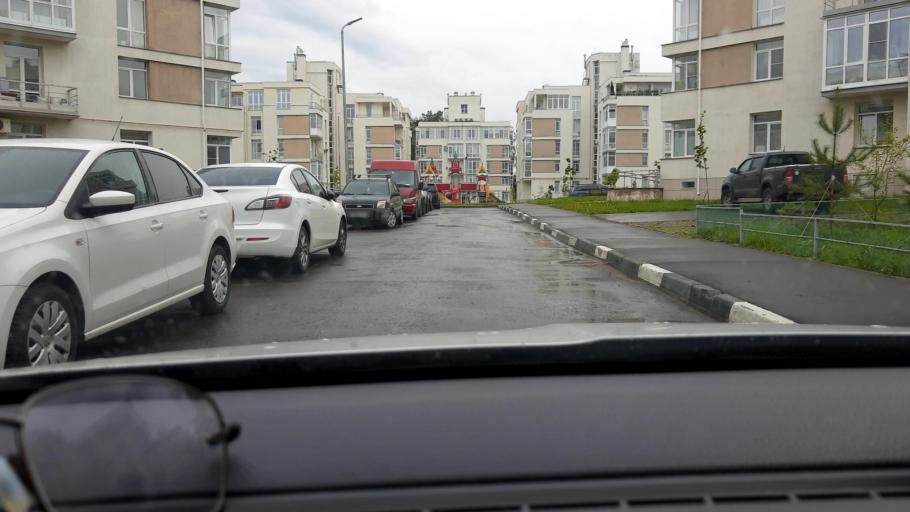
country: RU
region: Moskovskaya
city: Skhodnya
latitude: 55.8986
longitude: 37.2809
